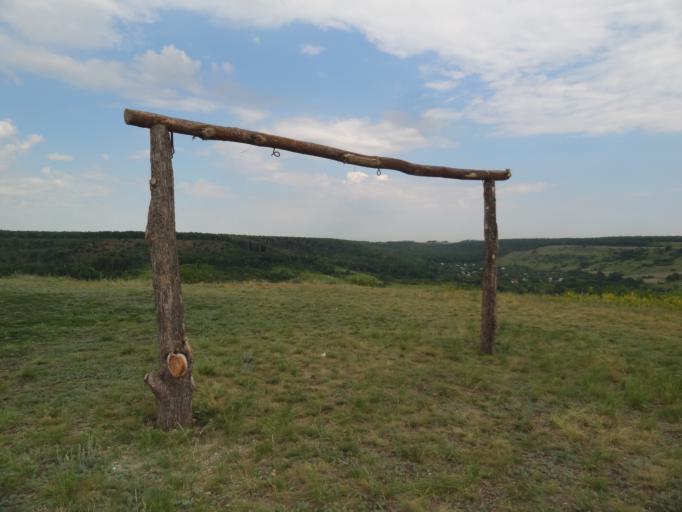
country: RU
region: Saratov
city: Krasnyy Oktyabr'
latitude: 51.4380
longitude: 45.7884
